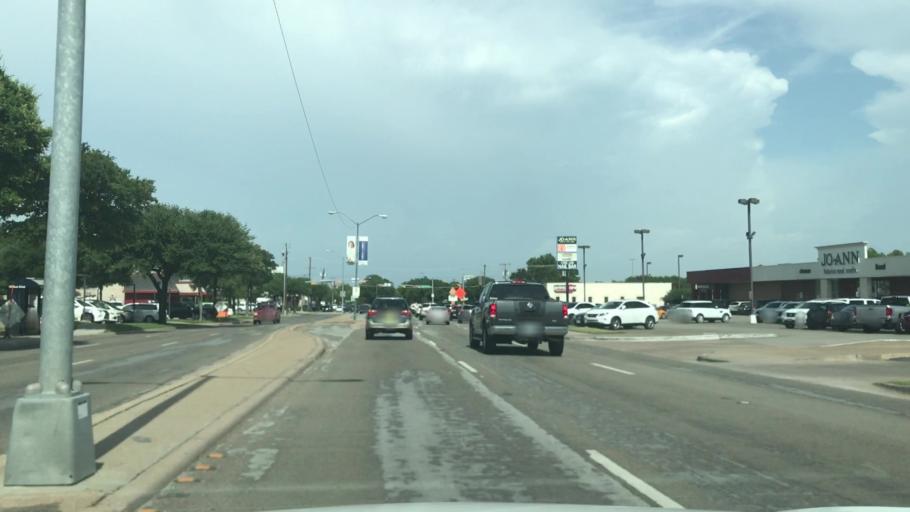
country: US
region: Texas
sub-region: Dallas County
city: Highland Park
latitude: 32.8365
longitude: -96.7550
